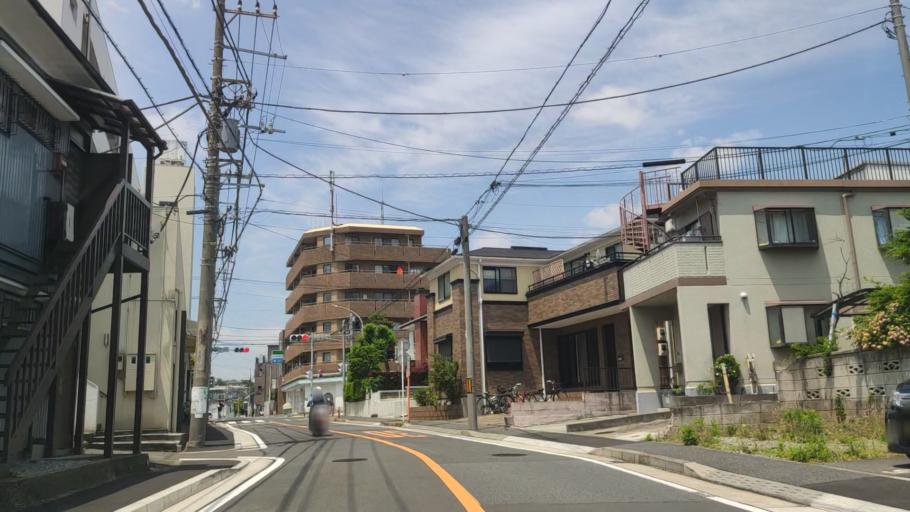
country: JP
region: Kanagawa
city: Yokohama
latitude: 35.4191
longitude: 139.6676
